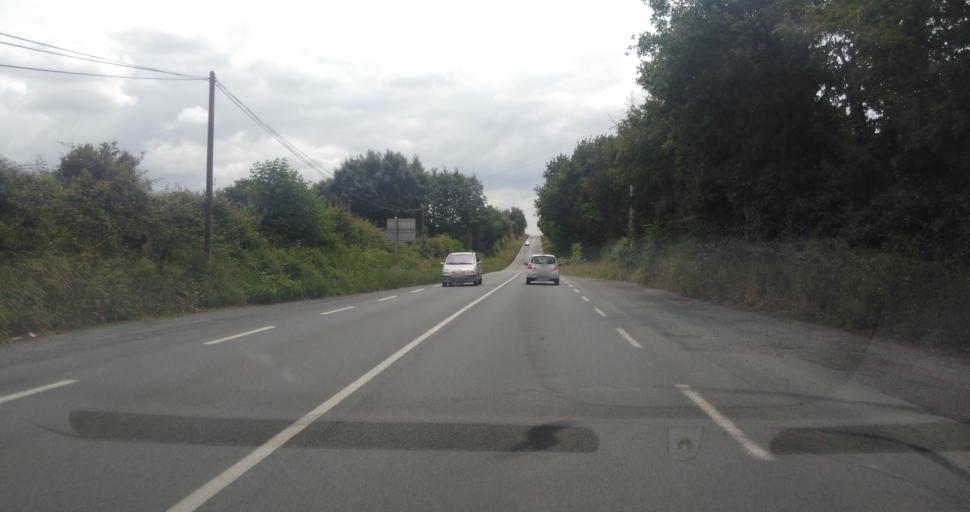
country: FR
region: Pays de la Loire
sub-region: Departement de la Vendee
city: Bournezeau
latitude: 46.6261
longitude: -1.1601
